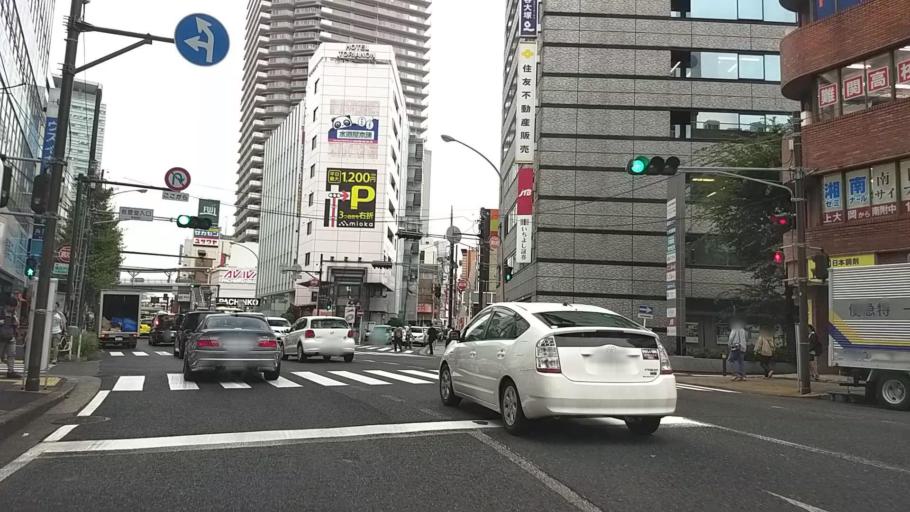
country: JP
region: Kanagawa
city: Yokohama
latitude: 35.4106
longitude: 139.5961
